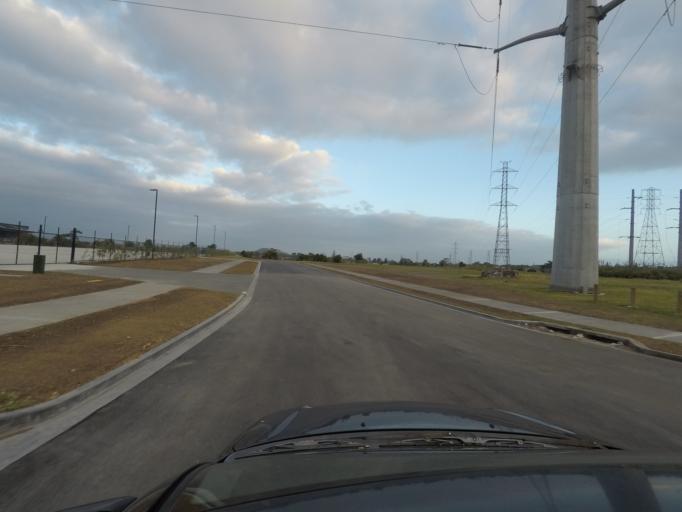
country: NZ
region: Auckland
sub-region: Auckland
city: Tamaki
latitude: -36.9297
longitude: 174.8739
